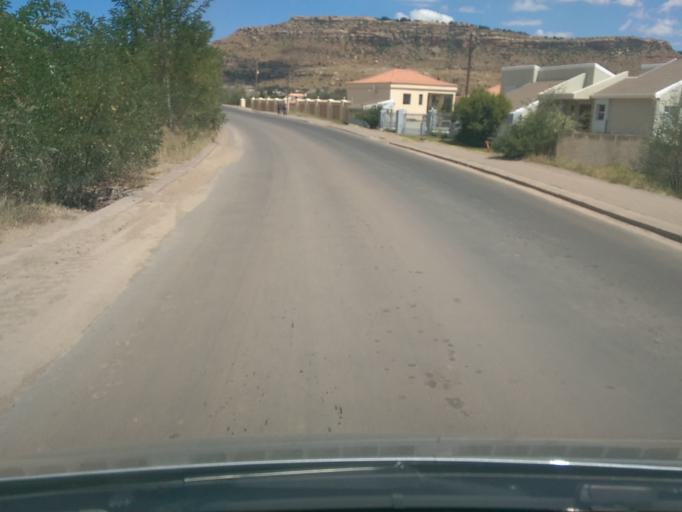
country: LS
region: Maseru
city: Maseru
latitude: -29.3220
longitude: 27.4829
